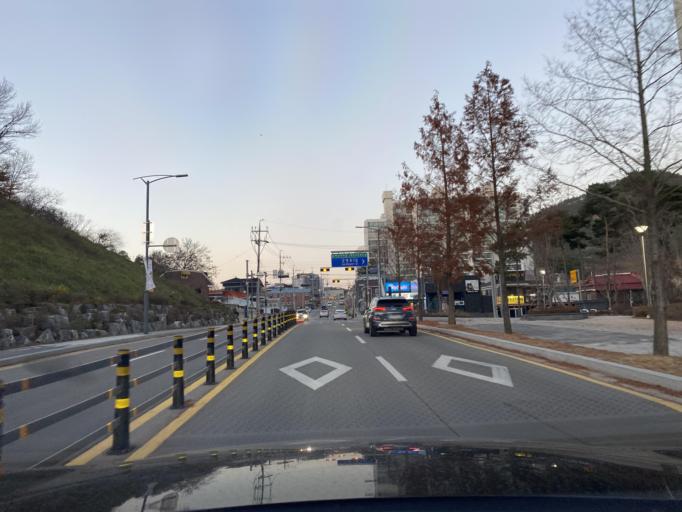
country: KR
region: Chungcheongnam-do
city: Yesan
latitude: 36.6822
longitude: 126.8436
